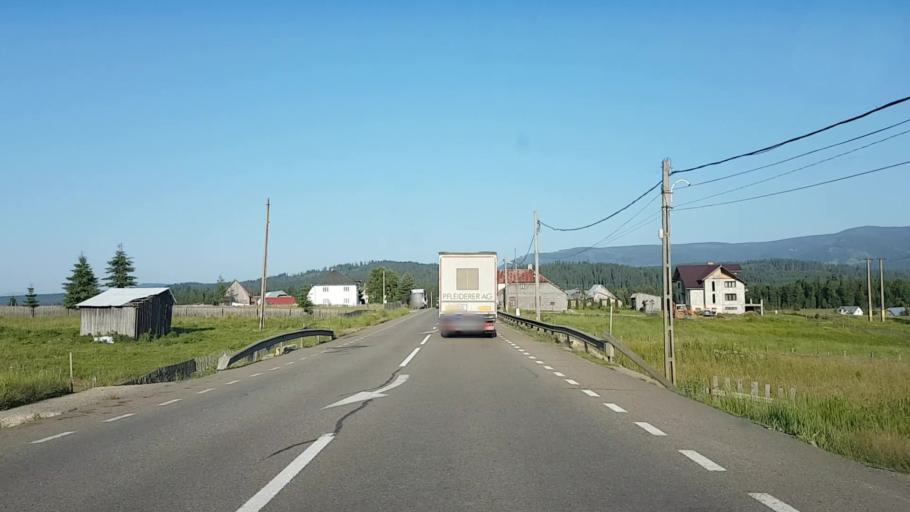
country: RO
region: Suceava
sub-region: Comuna Poiana Stampei
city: Poiana Stampei
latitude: 47.3004
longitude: 25.1023
